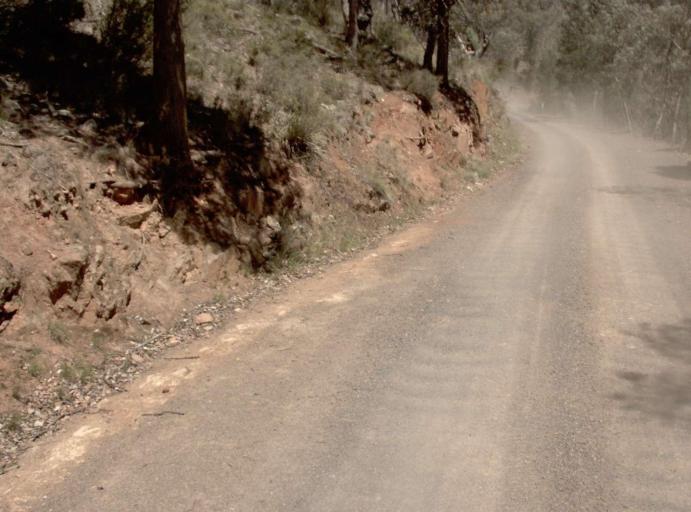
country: AU
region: New South Wales
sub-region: Snowy River
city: Jindabyne
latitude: -37.0641
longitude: 148.5044
